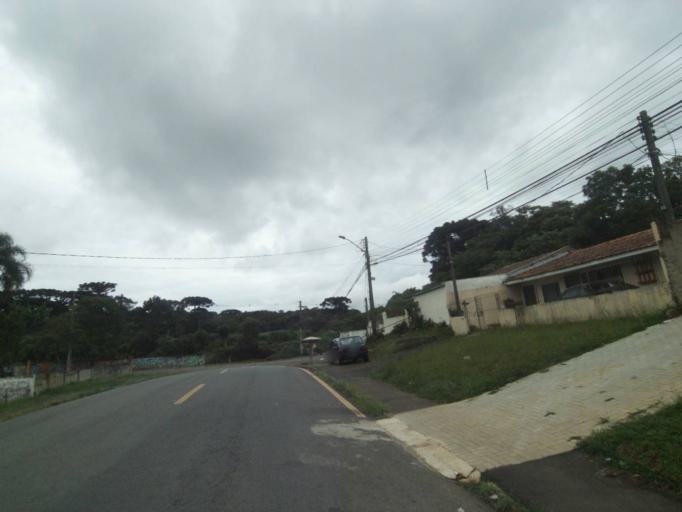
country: BR
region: Parana
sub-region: Curitiba
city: Curitiba
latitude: -25.4543
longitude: -49.3239
